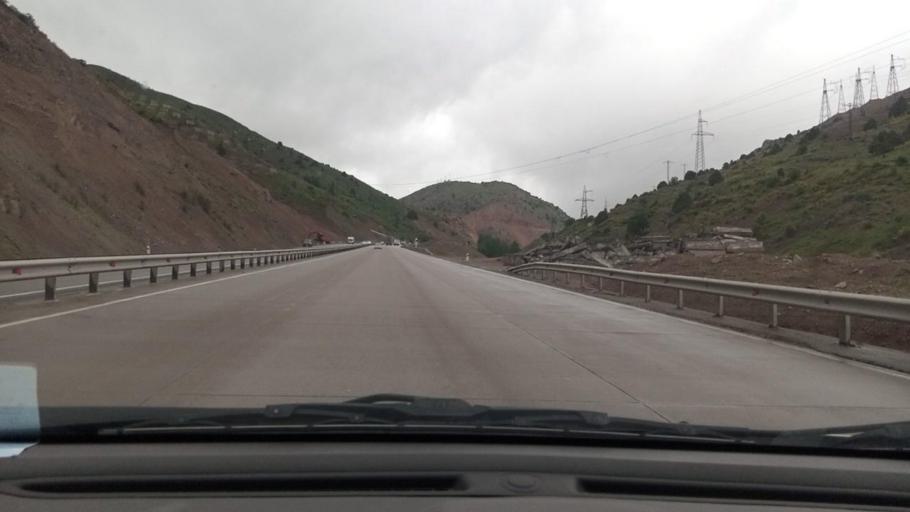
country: UZ
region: Toshkent
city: Angren
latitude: 41.0570
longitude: 70.5635
